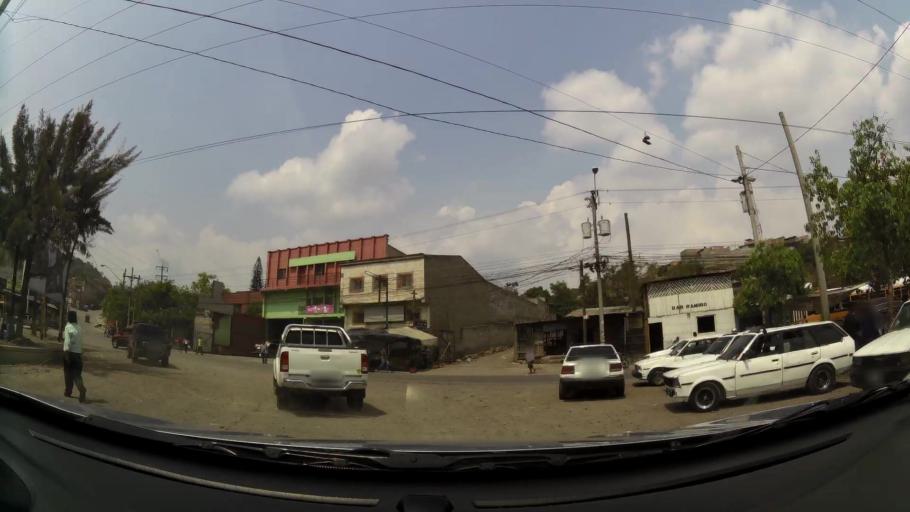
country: HN
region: Francisco Morazan
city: Tegucigalpa
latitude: 14.1053
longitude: -87.2325
